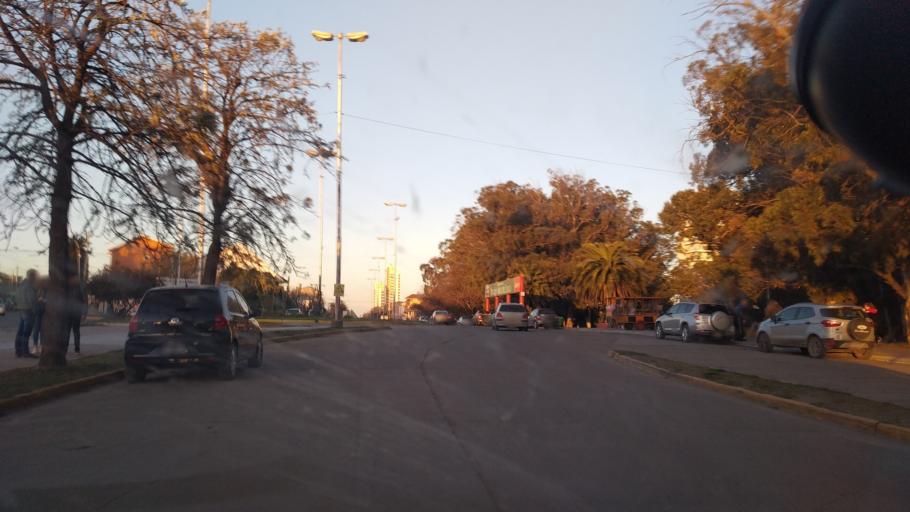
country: AR
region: Buenos Aires
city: Necochea
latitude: -38.5807
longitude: -58.7375
